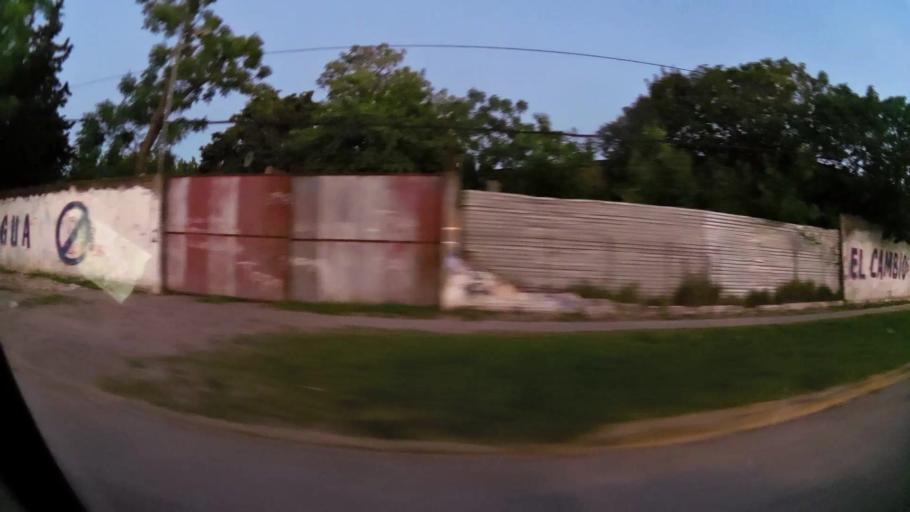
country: AR
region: Buenos Aires
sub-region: Partido de Quilmes
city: Quilmes
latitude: -34.7858
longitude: -58.1863
